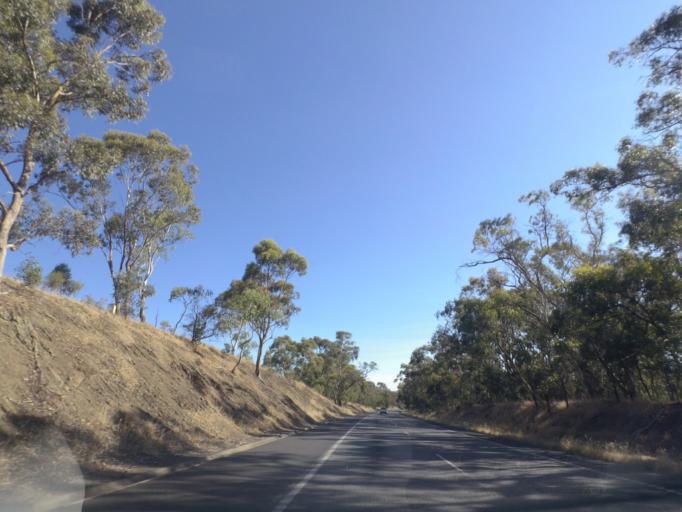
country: AU
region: Victoria
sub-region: Murrindindi
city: Kinglake West
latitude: -37.1690
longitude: 145.0771
